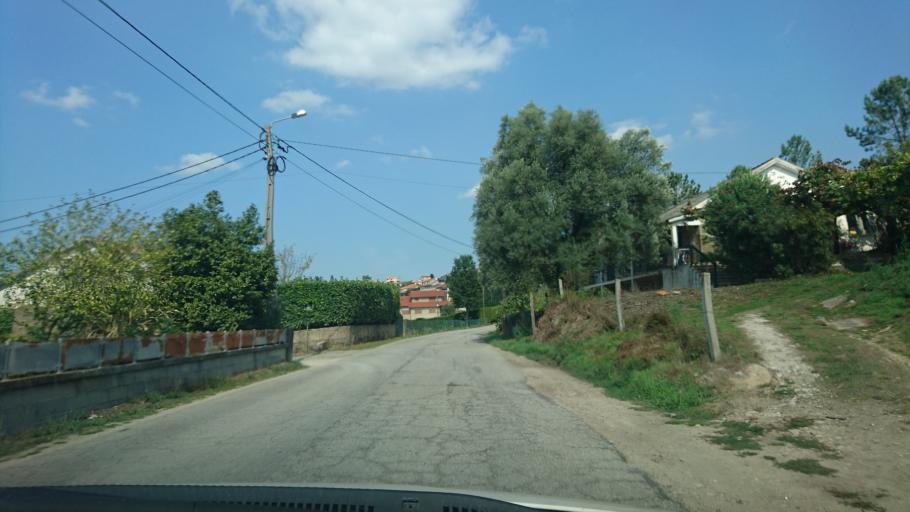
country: PT
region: Vila Real
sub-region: Mondim de Basto
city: Mondim de Basto
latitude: 41.4332
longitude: -7.9285
